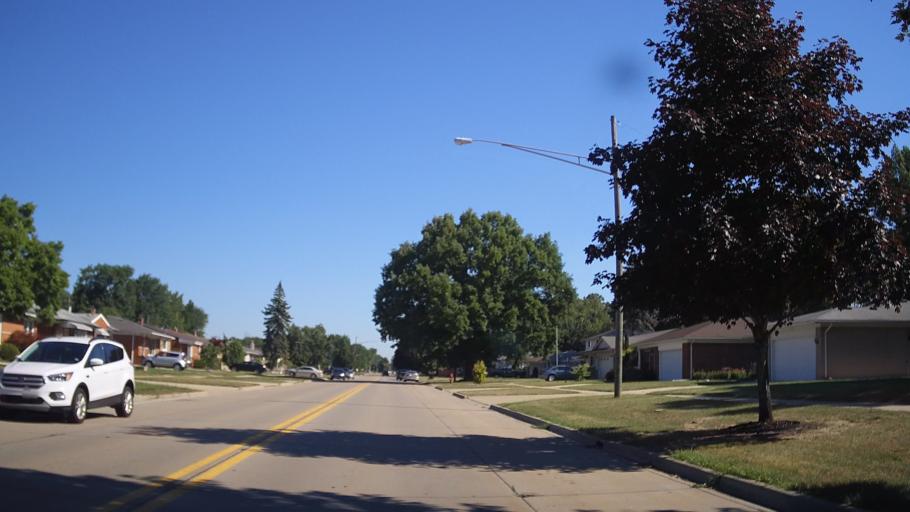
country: US
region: Michigan
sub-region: Macomb County
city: Fraser
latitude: 42.5273
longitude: -82.9292
